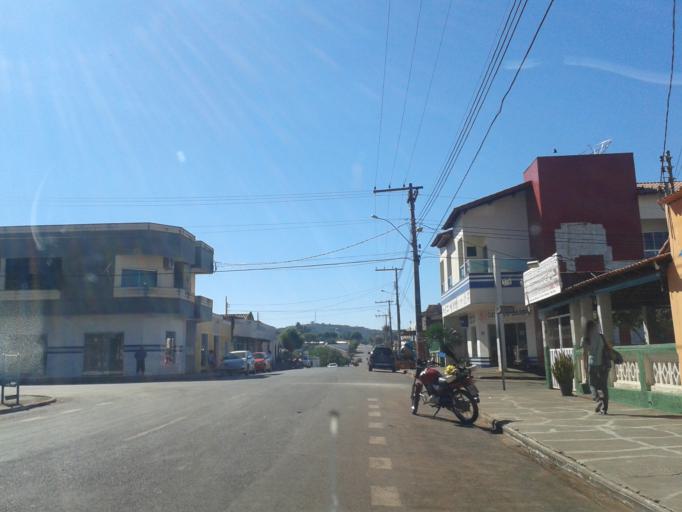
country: BR
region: Minas Gerais
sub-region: Ituiutaba
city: Ituiutaba
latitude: -19.2148
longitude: -49.7866
